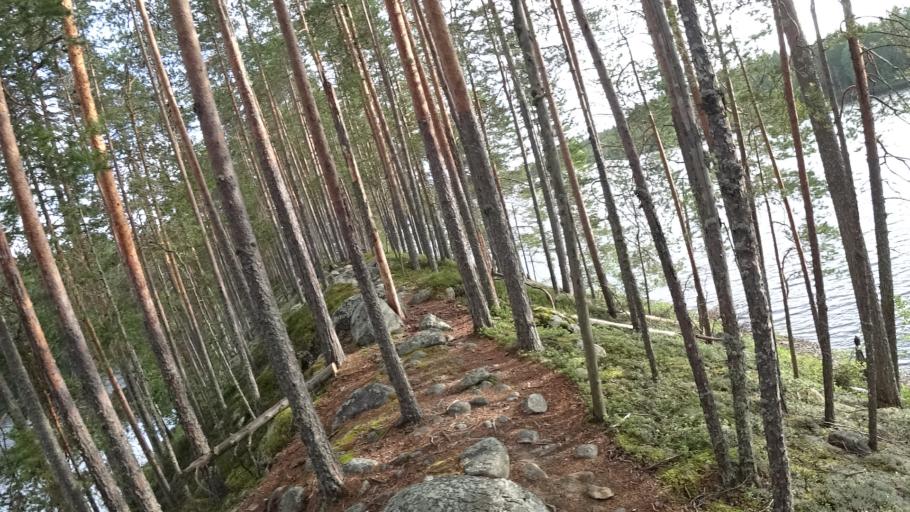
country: FI
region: North Karelia
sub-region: Joensuu
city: Ilomantsi
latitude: 62.5743
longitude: 31.1724
